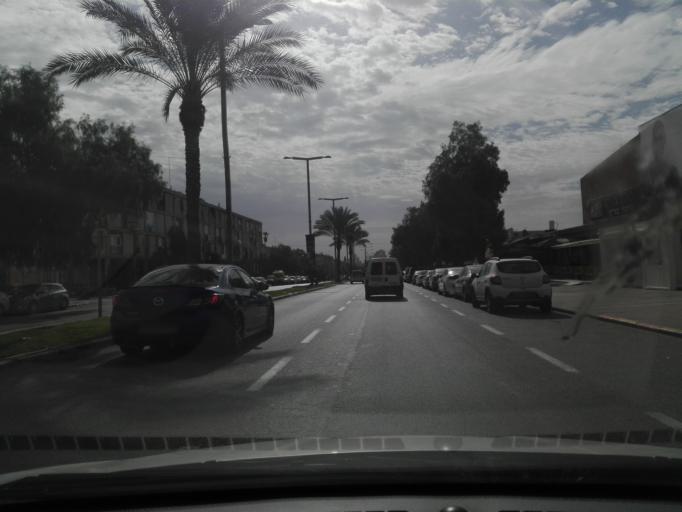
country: IL
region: Southern District
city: Beersheba
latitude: 31.2712
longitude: 34.7980
